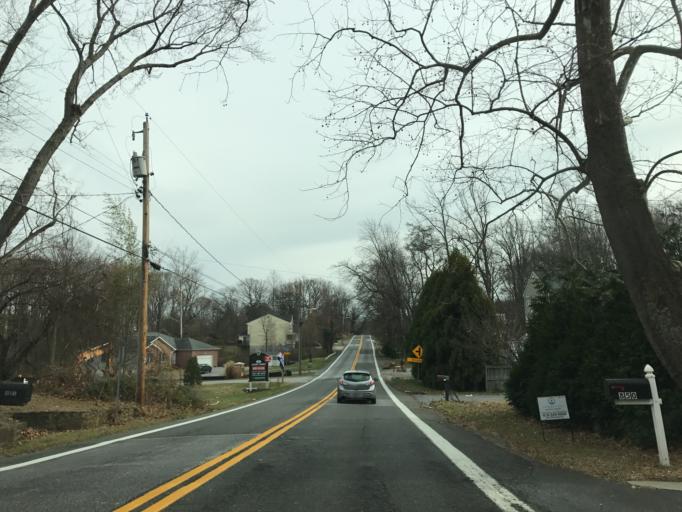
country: US
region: Maryland
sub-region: Anne Arundel County
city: Severna Park
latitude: 39.0619
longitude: -76.5366
